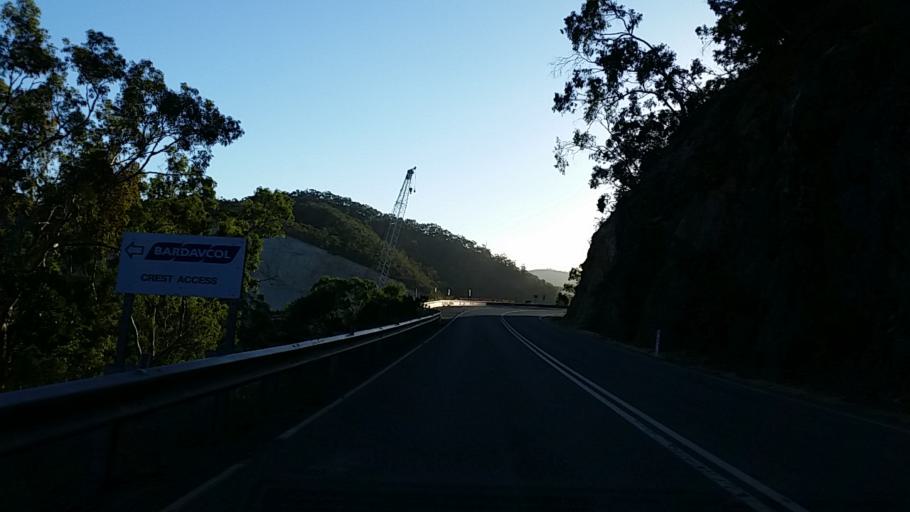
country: AU
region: South Australia
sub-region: Campbelltown
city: Athelstone
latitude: -34.8644
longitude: 138.7763
